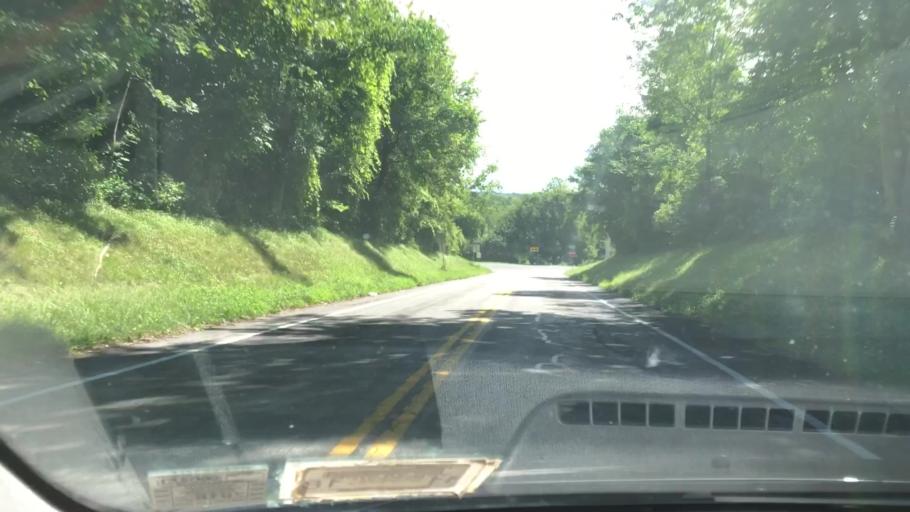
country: US
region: New York
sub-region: Monroe County
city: Fairport
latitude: 43.1090
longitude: -77.3744
